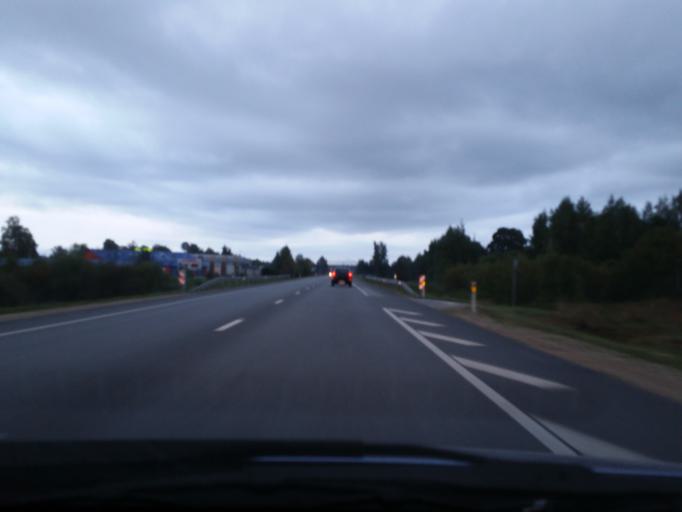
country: LV
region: Adazi
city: Adazi
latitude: 57.0830
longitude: 24.3153
